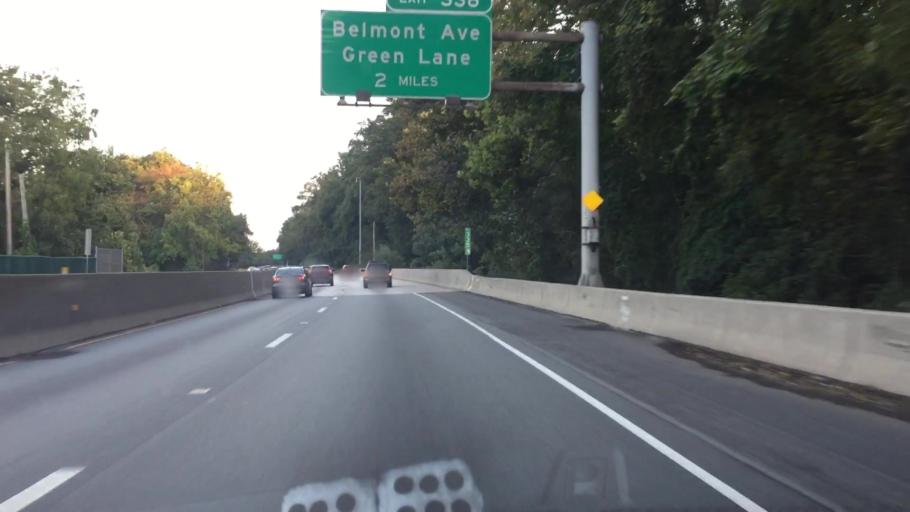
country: US
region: Pennsylvania
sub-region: Montgomery County
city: Narberth
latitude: 40.0455
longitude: -75.2580
